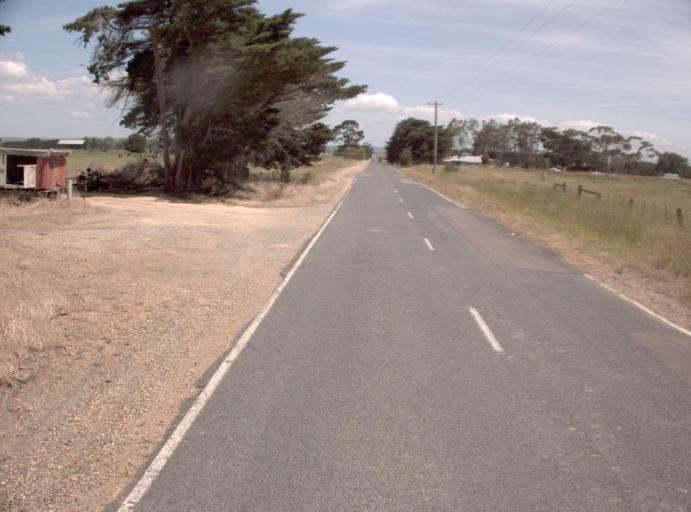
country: AU
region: Victoria
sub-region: Wellington
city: Heyfield
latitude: -38.0842
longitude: 146.8678
